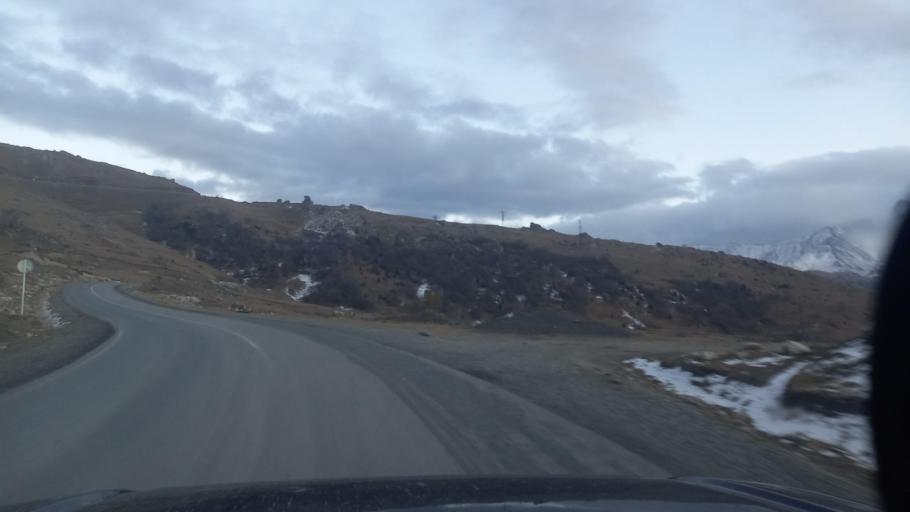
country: RU
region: Ingushetiya
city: Dzhayrakh
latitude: 42.8213
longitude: 44.8217
